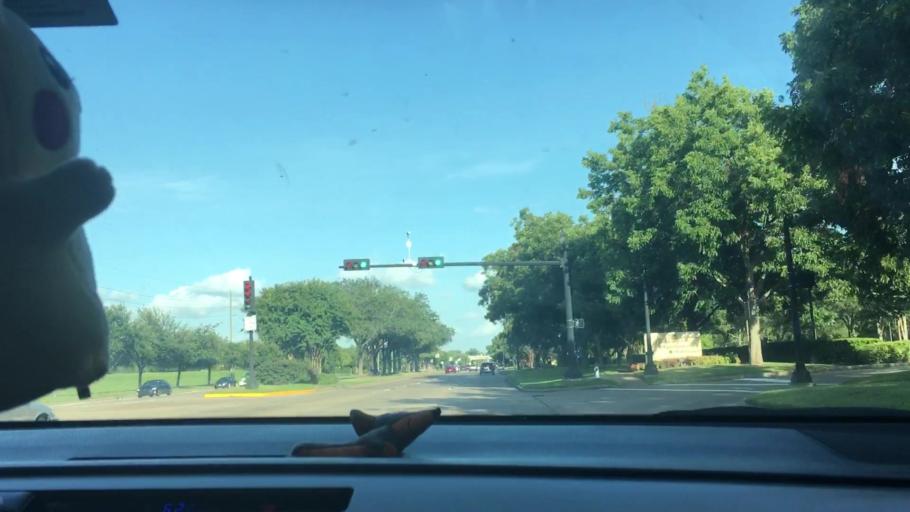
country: US
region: Texas
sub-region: Fort Bend County
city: Sugar Land
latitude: 29.6006
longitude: -95.6290
